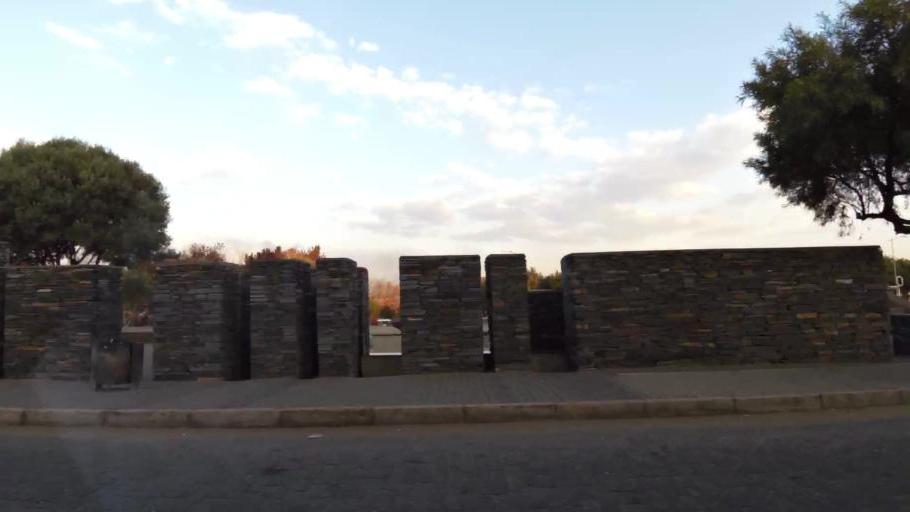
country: ZA
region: Gauteng
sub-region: City of Johannesburg Metropolitan Municipality
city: Soweto
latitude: -26.2351
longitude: 27.9079
